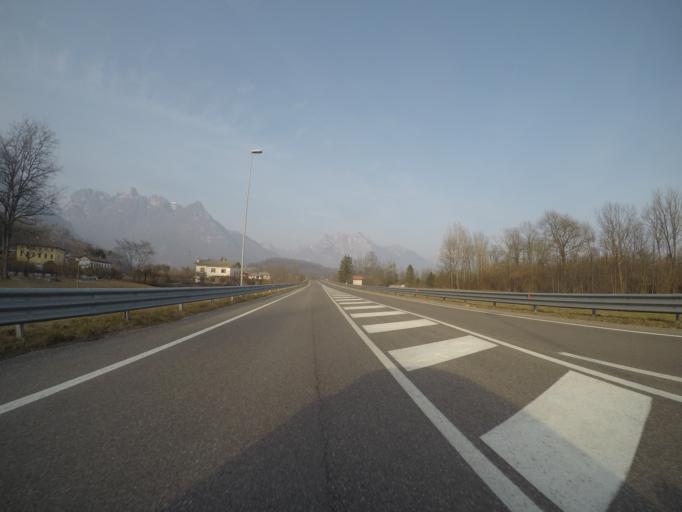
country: IT
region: Veneto
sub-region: Provincia di Belluno
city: Sospirolo
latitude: 46.1344
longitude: 12.0839
